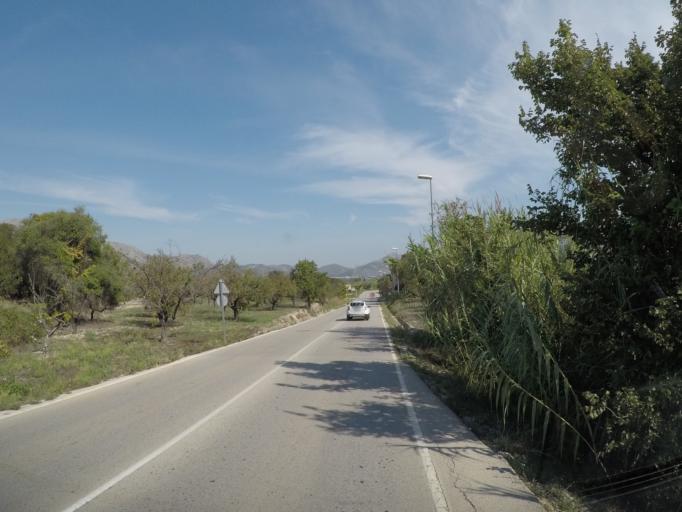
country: ES
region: Valencia
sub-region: Provincia de Alicante
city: Orba
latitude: 38.7793
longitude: -0.0663
